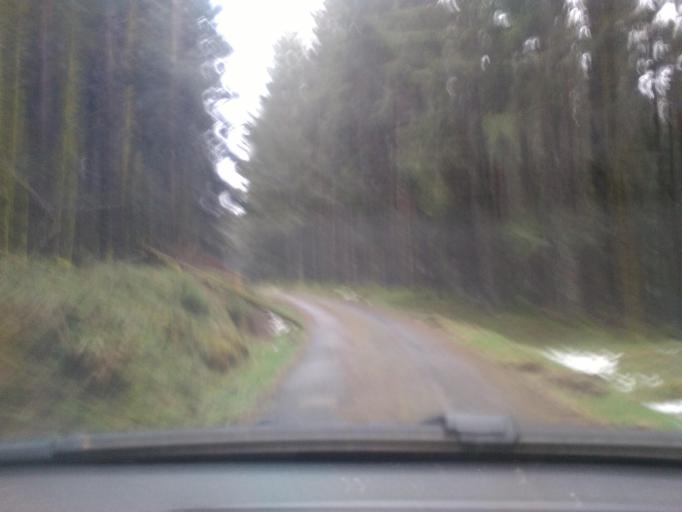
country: FR
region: Lorraine
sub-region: Departement des Vosges
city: Gerardmer
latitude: 48.1161
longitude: 6.8701
